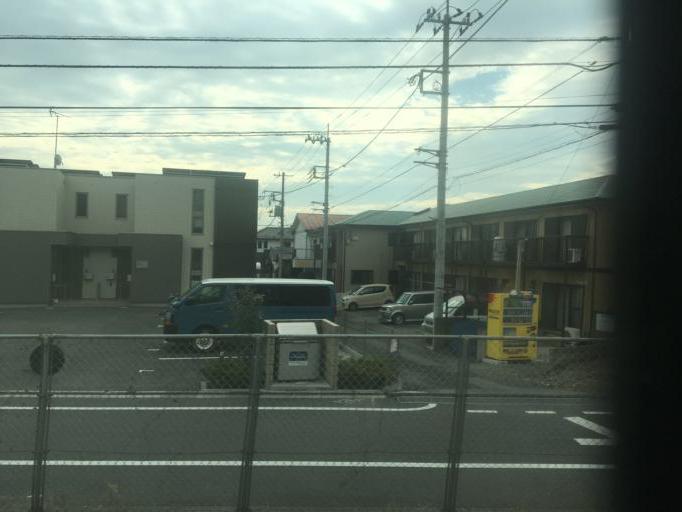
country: JP
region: Tokyo
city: Hino
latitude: 35.7114
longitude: 139.3681
